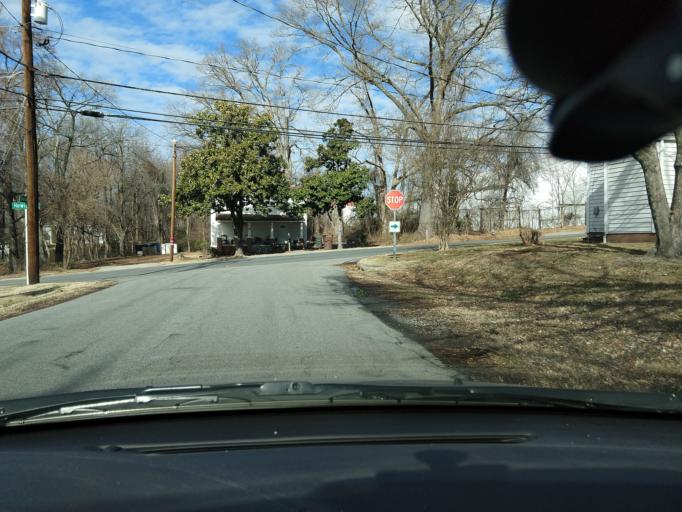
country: US
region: North Carolina
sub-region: Guilford County
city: Greensboro
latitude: 36.0563
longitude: -79.8656
